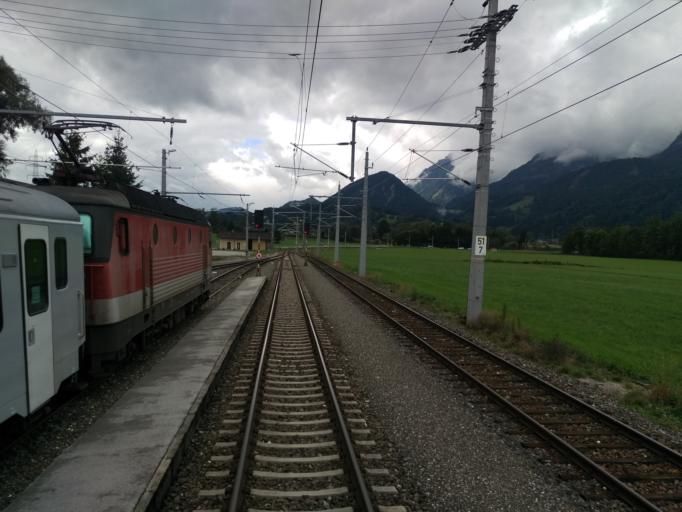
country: AT
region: Styria
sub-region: Politischer Bezirk Liezen
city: Aich
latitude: 47.4170
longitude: 13.7997
